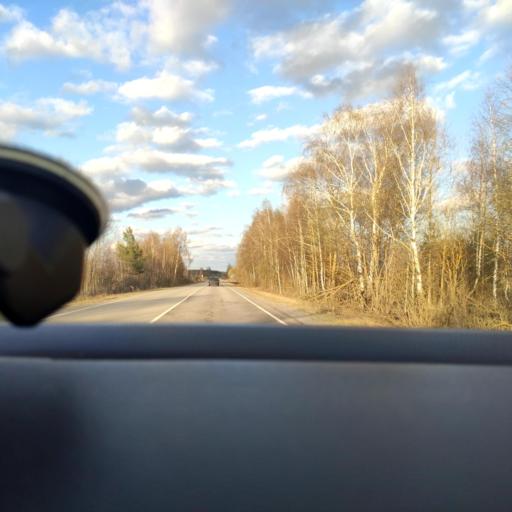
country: RU
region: Moskovskaya
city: Shaturtorf
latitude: 55.4311
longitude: 39.3963
